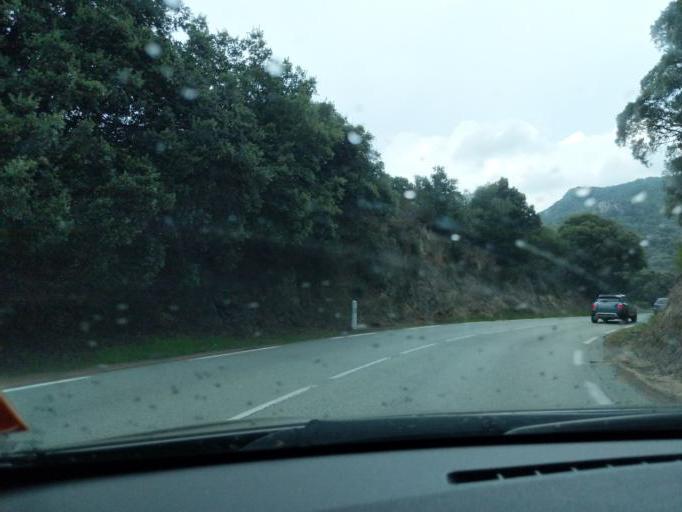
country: FR
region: Corsica
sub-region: Departement de la Corse-du-Sud
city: Sartene
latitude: 41.5873
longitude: 8.9382
